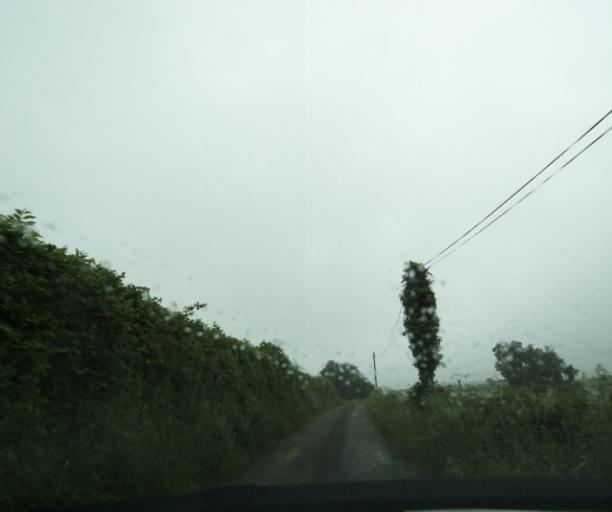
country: FR
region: Bourgogne
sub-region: Departement de Saone-et-Loire
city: Charolles
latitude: 46.4141
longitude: 4.3904
